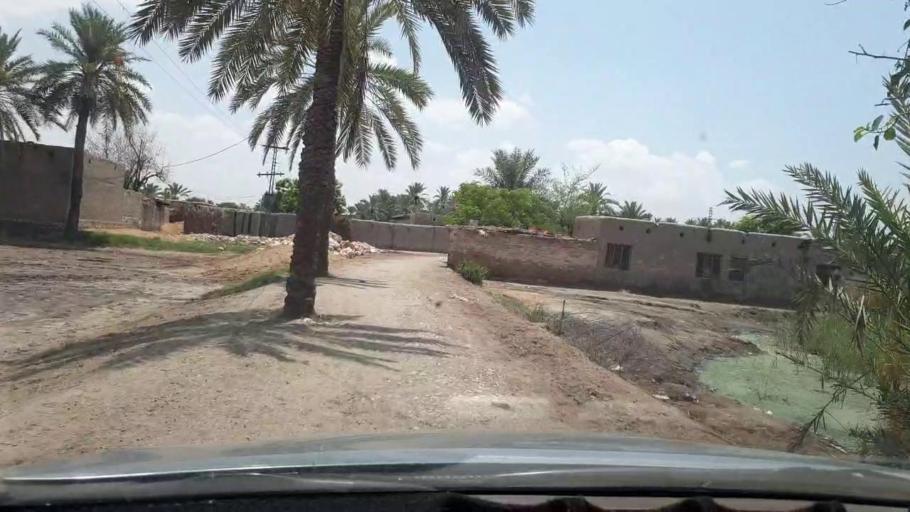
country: PK
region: Sindh
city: Khairpur
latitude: 27.4429
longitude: 68.7919
